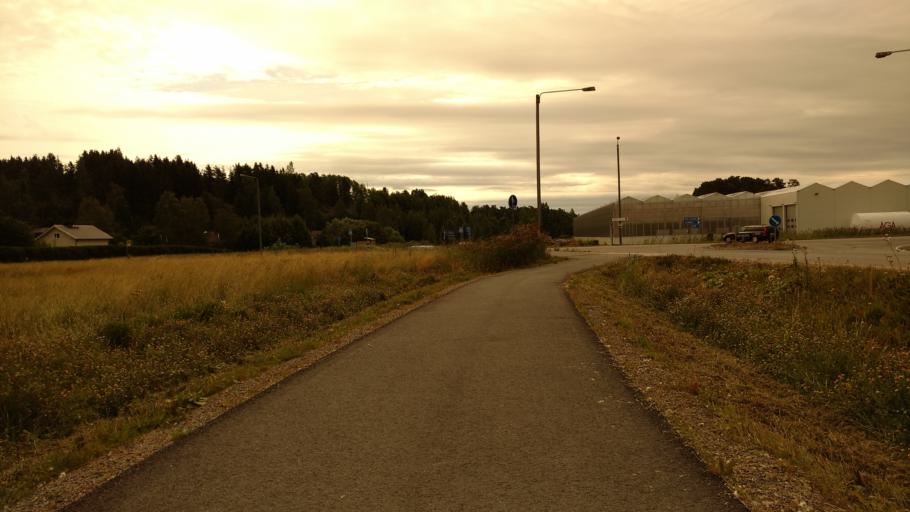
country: FI
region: Varsinais-Suomi
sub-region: Turku
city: Piikkioe
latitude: 60.4263
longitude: 22.4857
